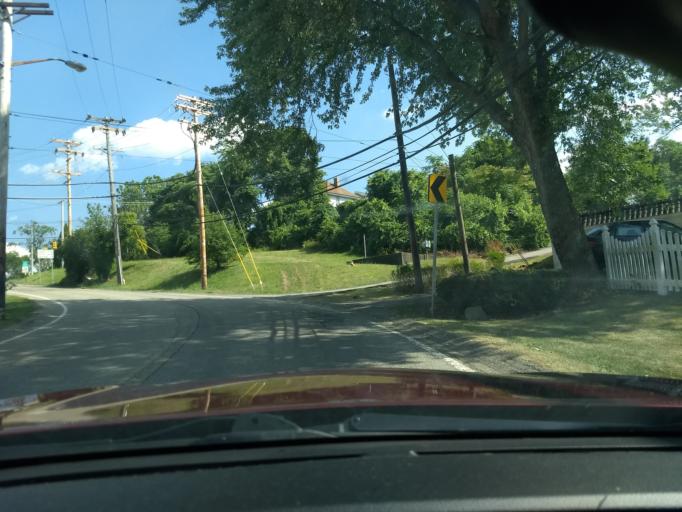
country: US
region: Pennsylvania
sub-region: Allegheny County
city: West Homestead
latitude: 40.3773
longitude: -79.9101
